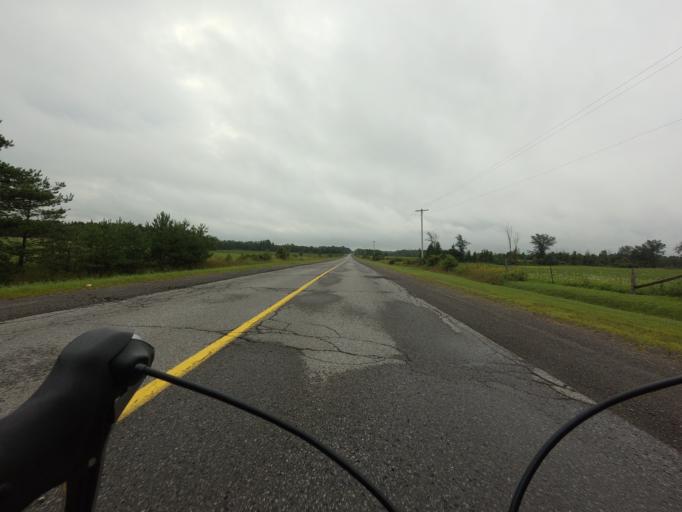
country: CA
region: Ontario
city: Bells Corners
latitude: 45.1592
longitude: -75.7933
